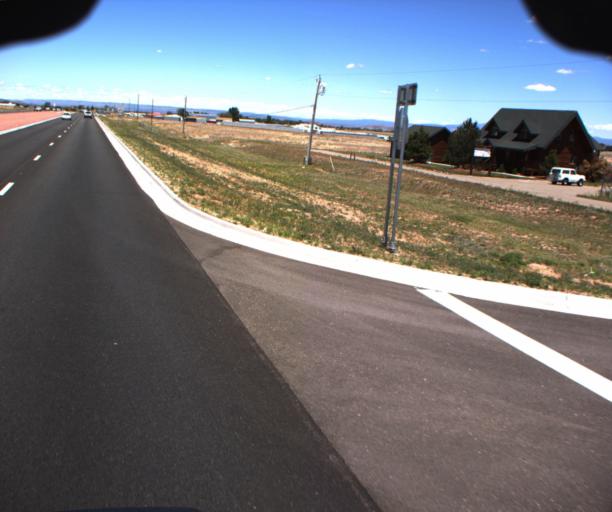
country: US
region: Arizona
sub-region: Yavapai County
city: Chino Valley
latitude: 34.7072
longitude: -112.4509
